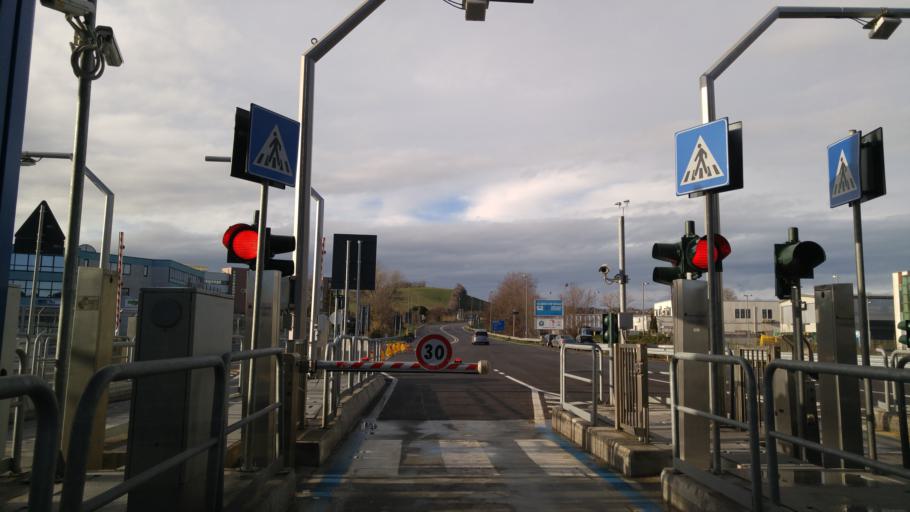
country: IT
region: The Marches
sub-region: Provincia di Ancona
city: San Biagio
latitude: 43.5301
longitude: 13.5148
